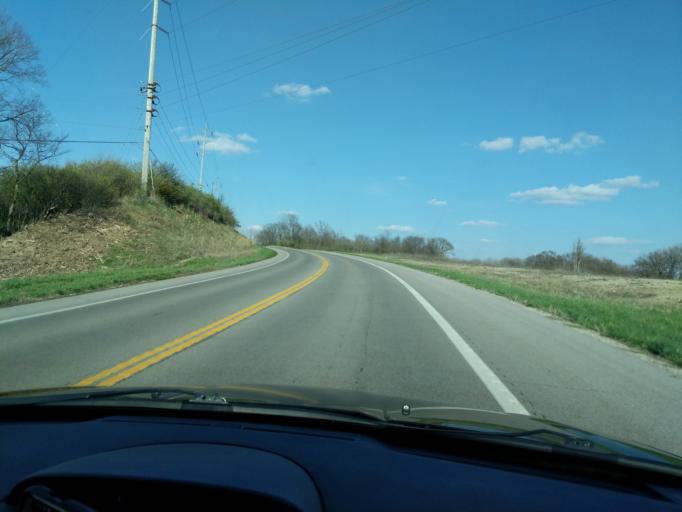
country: US
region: Ohio
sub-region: Champaign County
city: Urbana
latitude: 40.1066
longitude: -83.7837
